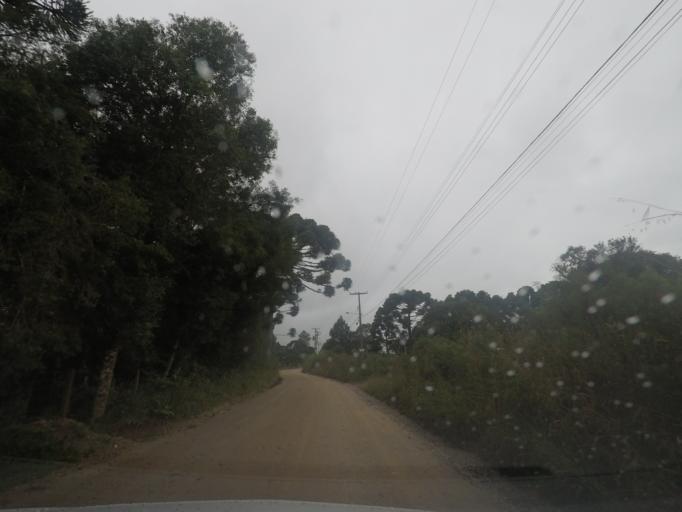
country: BR
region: Parana
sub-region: Campina Grande Do Sul
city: Campina Grande do Sul
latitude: -25.3131
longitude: -49.0835
